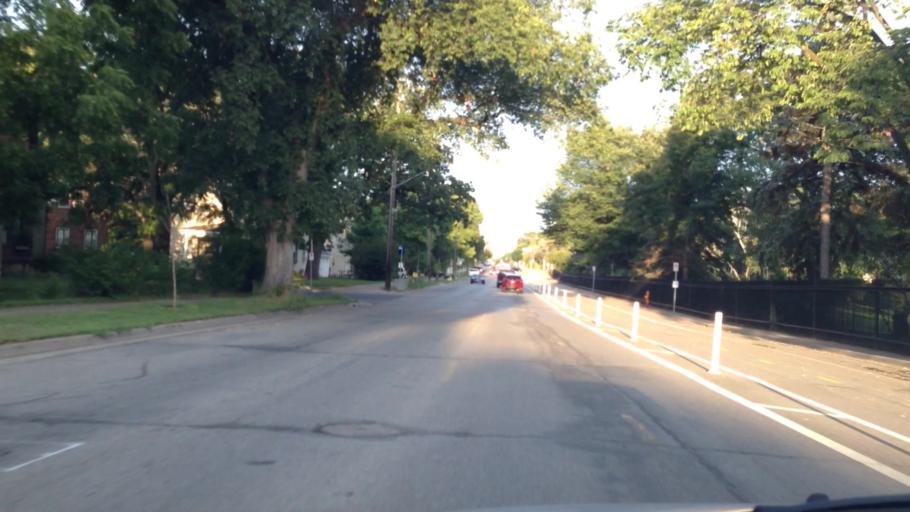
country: US
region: Minnesota
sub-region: Hennepin County
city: Saint Louis Park
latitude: 44.9377
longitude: -93.2965
